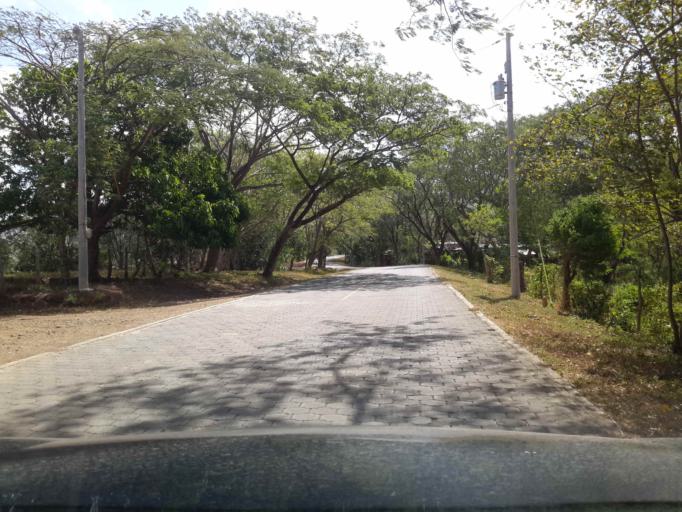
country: NI
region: Rivas
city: San Juan del Sur
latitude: 11.2447
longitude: -85.8373
